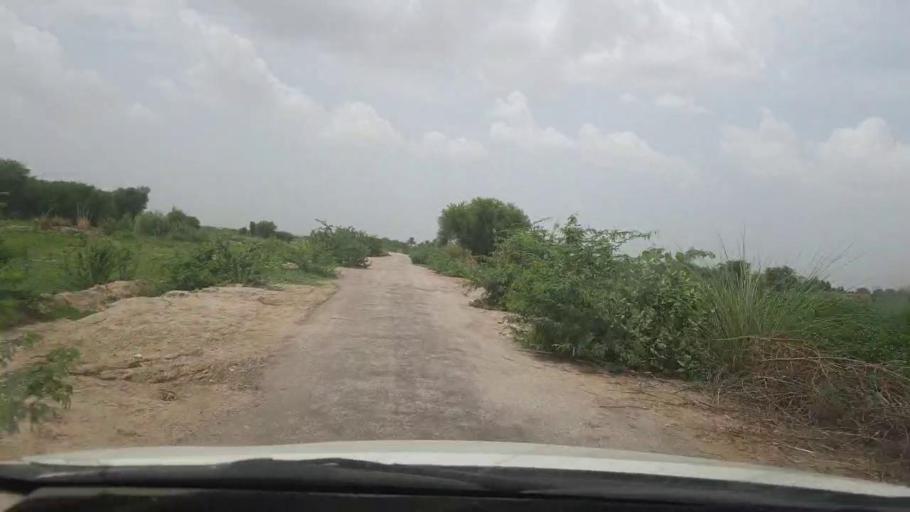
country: PK
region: Sindh
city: Khairpur
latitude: 27.3944
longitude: 68.9878
